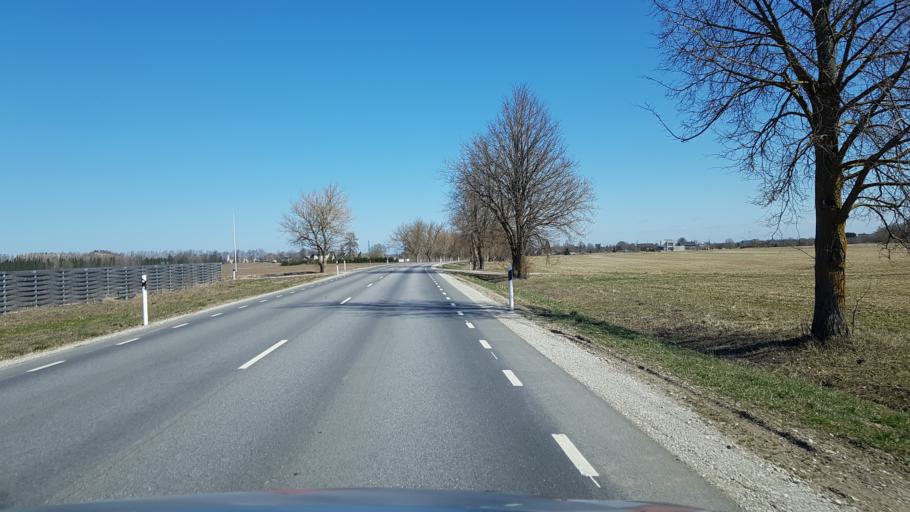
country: EE
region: Ida-Virumaa
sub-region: Johvi vald
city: Johvi
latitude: 59.3473
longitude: 27.3696
